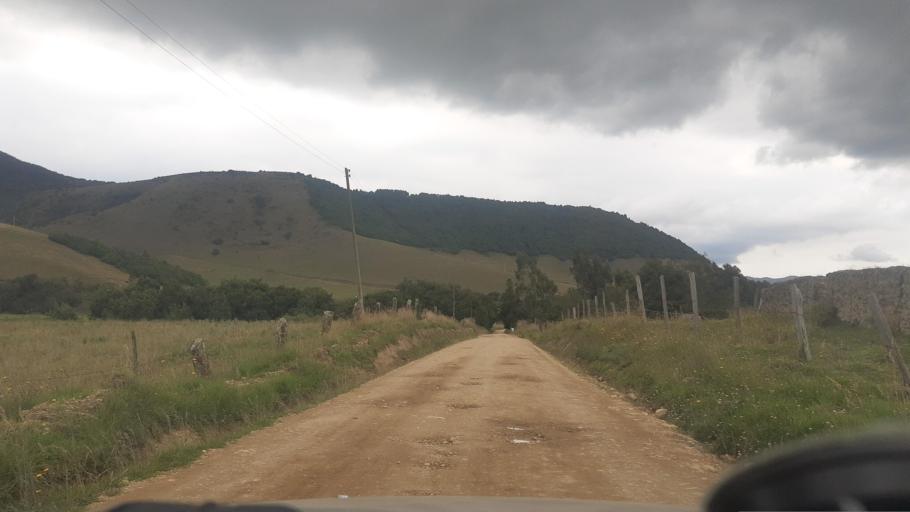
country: CO
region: Cundinamarca
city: Suesca
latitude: 5.1528
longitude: -73.7959
